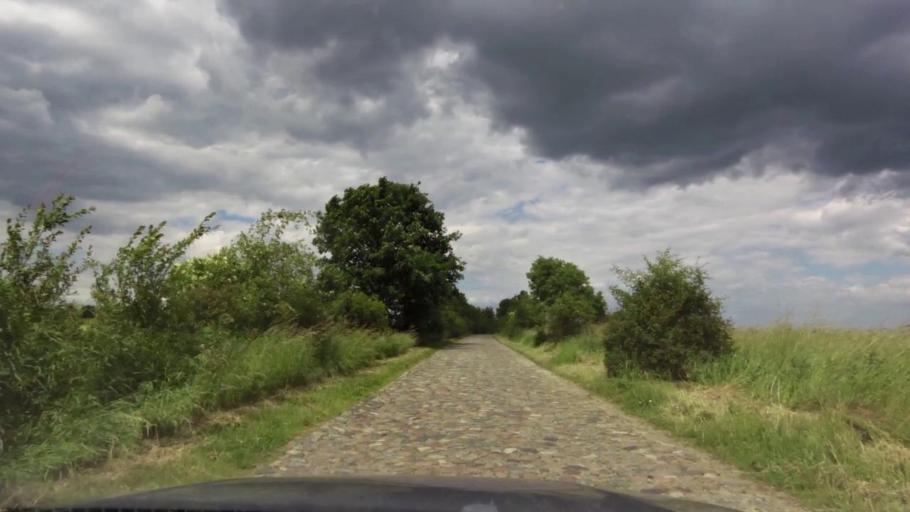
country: PL
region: West Pomeranian Voivodeship
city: Trzcinsko Zdroj
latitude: 52.9539
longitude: 14.7142
